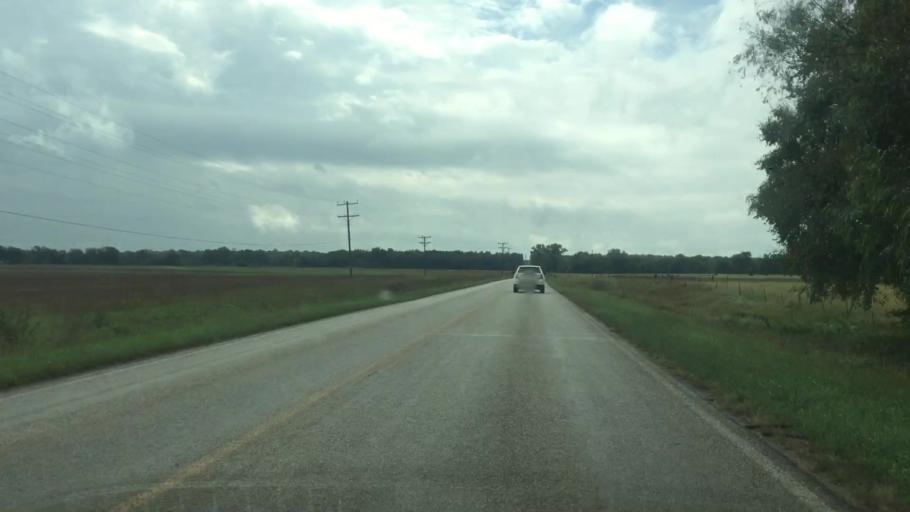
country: US
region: Kansas
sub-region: Allen County
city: Iola
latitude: 37.8772
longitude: -95.4369
